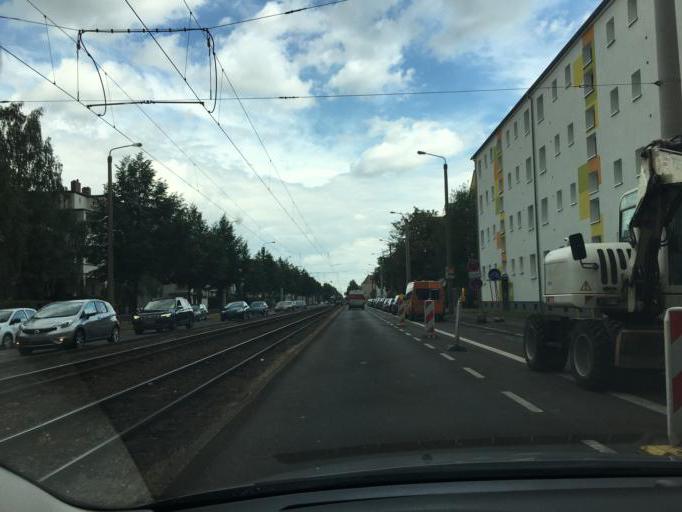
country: DE
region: Saxony-Anhalt
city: Halle (Saale)
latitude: 51.4567
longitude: 11.9676
